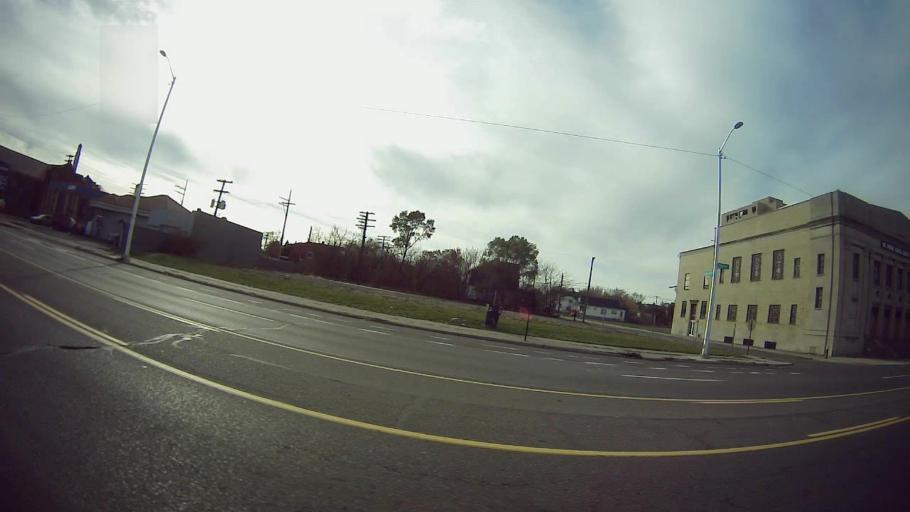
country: US
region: Michigan
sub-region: Wayne County
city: Highland Park
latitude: 42.3774
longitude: -83.1225
